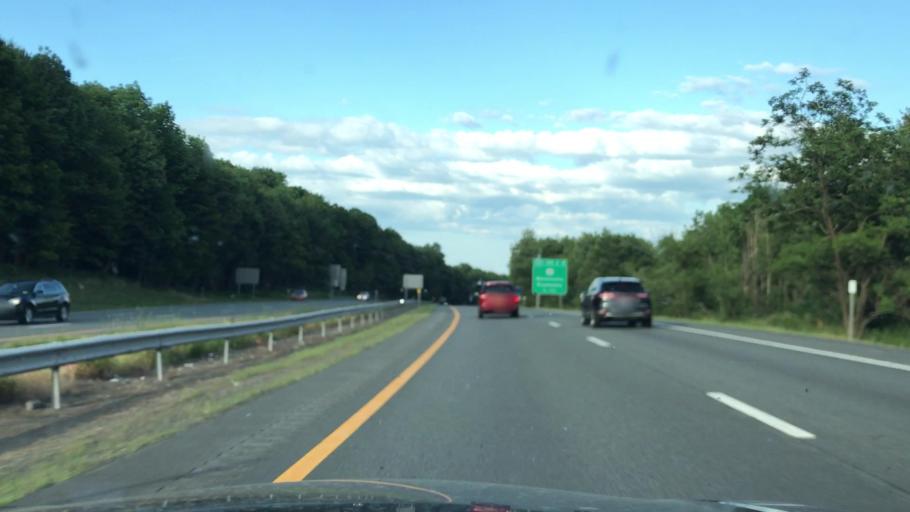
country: US
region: New York
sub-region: Sullivan County
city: Monticello
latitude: 41.6636
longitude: -74.6888
